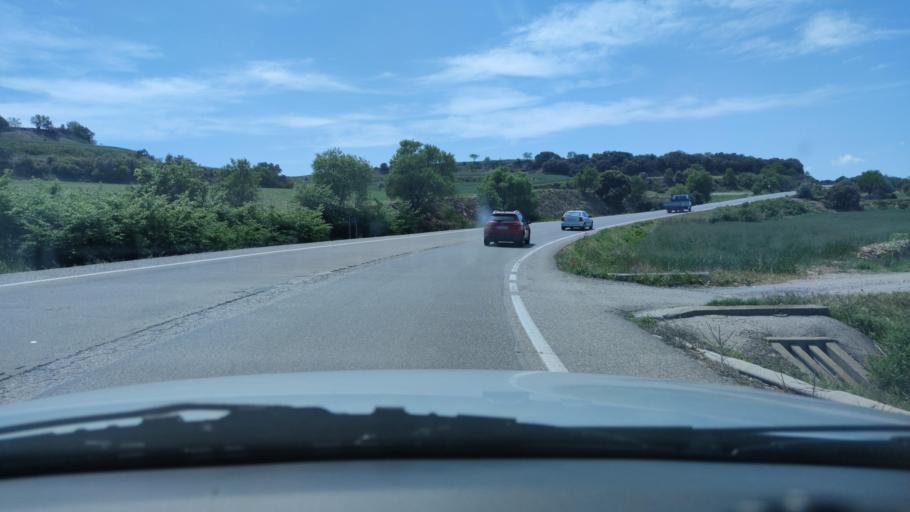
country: ES
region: Catalonia
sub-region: Provincia de Lleida
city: Tarrega
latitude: 41.6798
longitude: 1.1637
